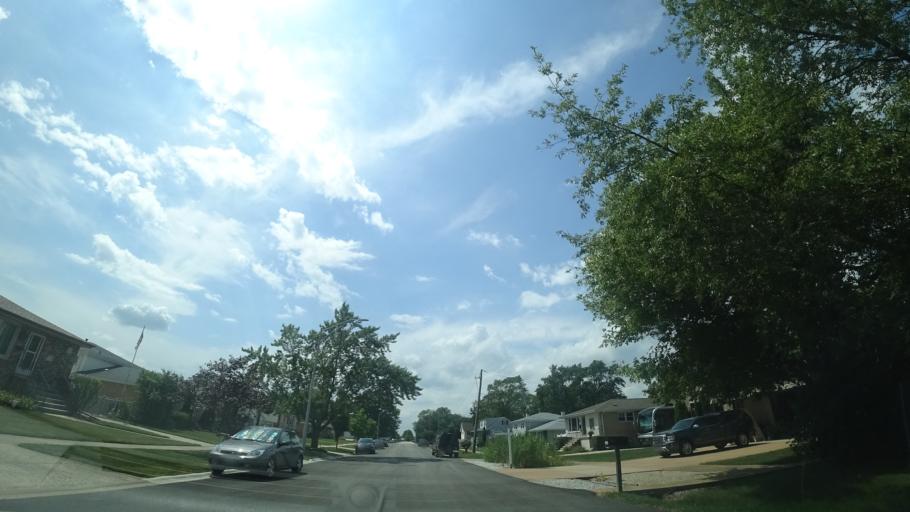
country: US
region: Illinois
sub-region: Cook County
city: Alsip
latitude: 41.6736
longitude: -87.7457
